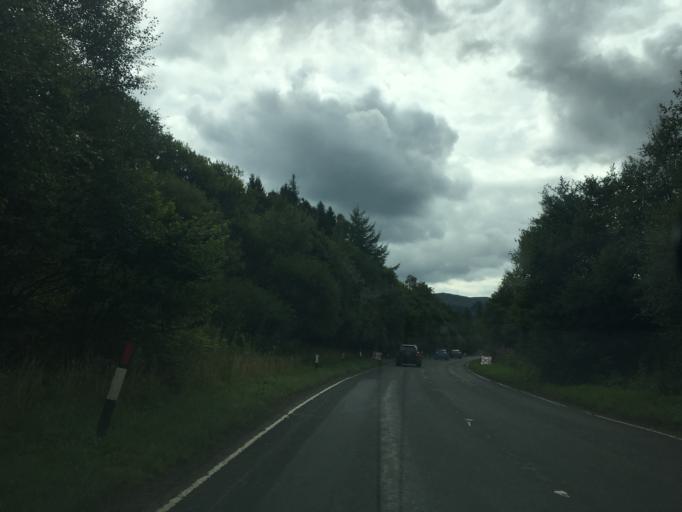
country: GB
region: Scotland
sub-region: Stirling
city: Callander
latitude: 56.3346
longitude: -4.3240
